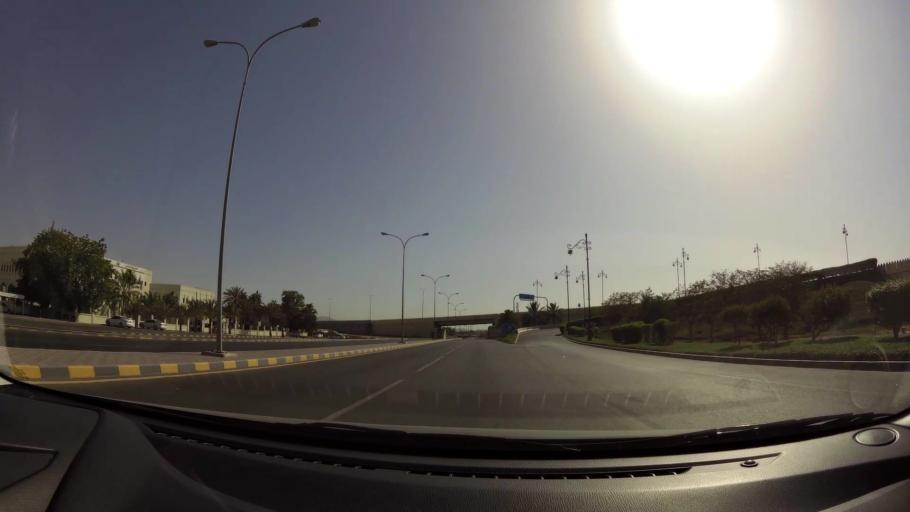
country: OM
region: Muhafazat Masqat
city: Bawshar
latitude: 23.5842
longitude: 58.2960
